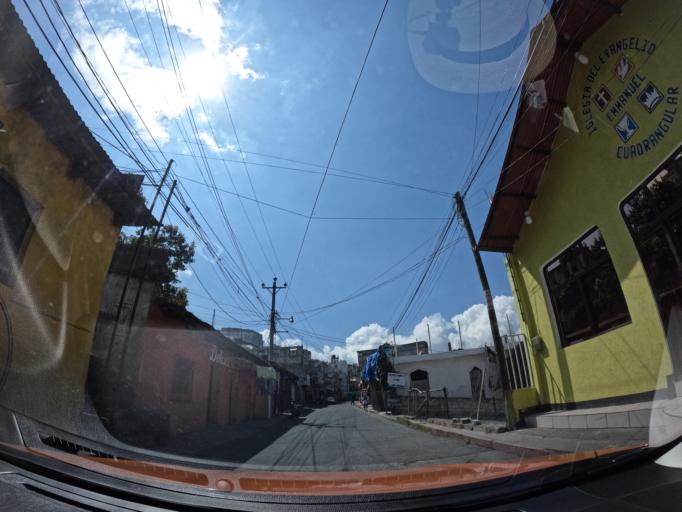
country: GT
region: Solola
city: Santiago Atitlan
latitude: 14.6418
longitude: -91.2286
